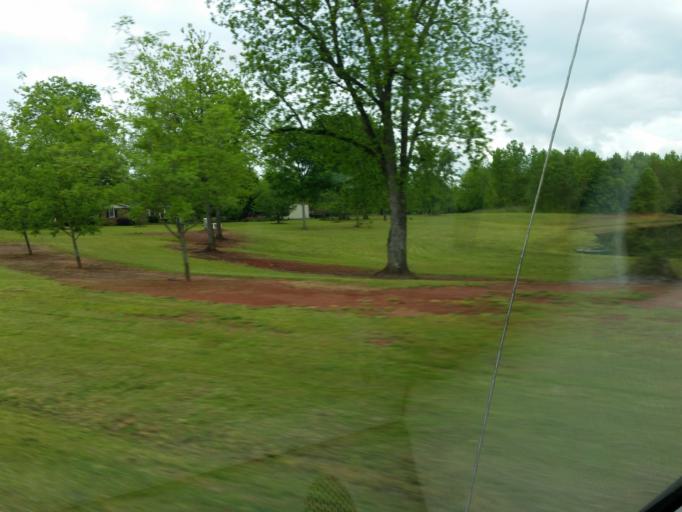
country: US
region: Georgia
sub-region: Peach County
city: Byron
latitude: 32.6802
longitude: -83.8500
